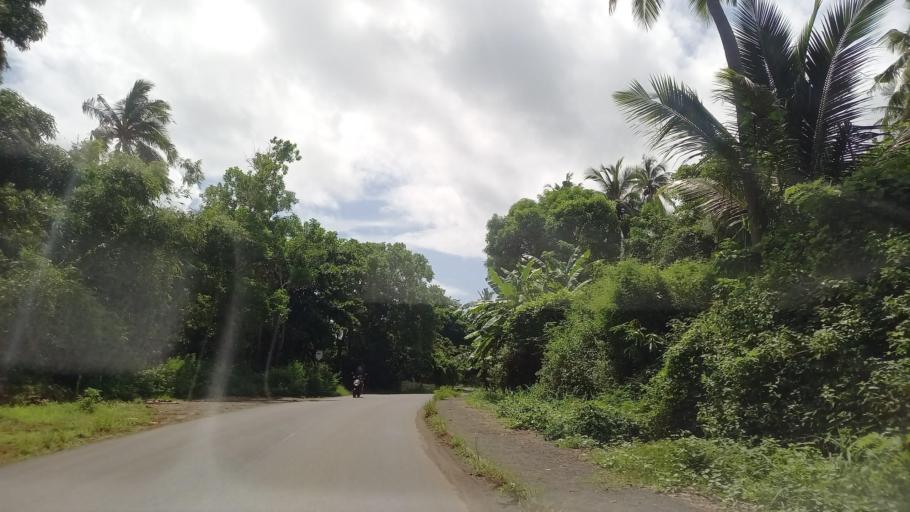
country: YT
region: Boueni
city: Boueni
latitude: -12.9196
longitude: 45.0830
